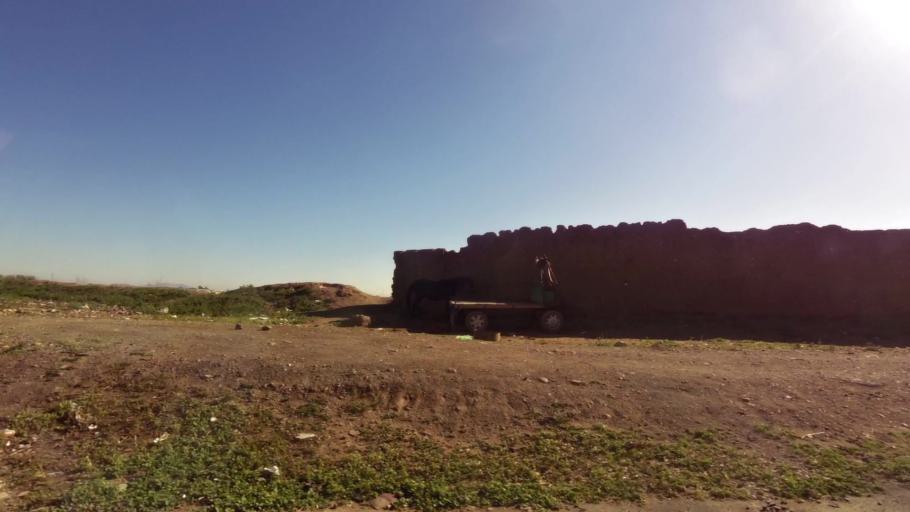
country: MA
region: Marrakech-Tensift-Al Haouz
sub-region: Marrakech
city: Marrakesh
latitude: 31.6016
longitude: -8.0313
